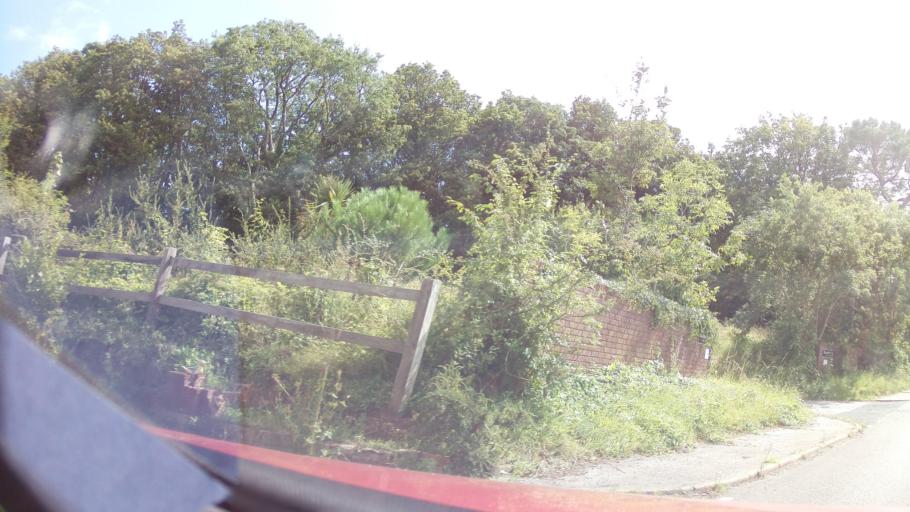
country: GB
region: England
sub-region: Borough of Torbay
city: Torquay
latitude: 50.5056
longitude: -3.5254
